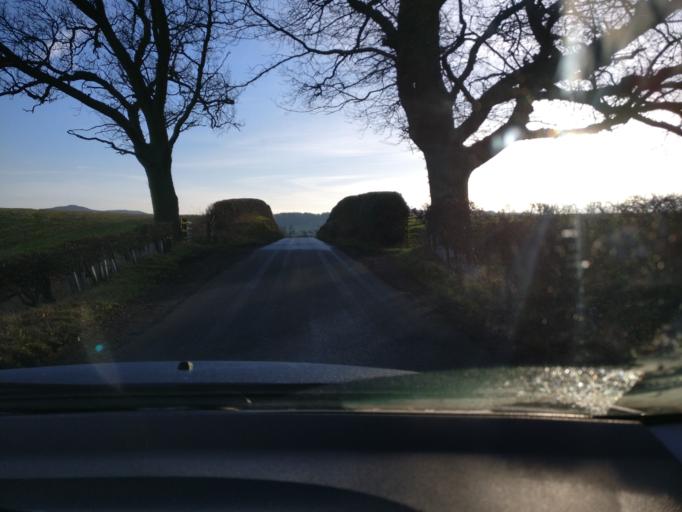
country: GB
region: Scotland
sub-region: The Scottish Borders
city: Hawick
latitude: 55.4446
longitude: -2.7527
